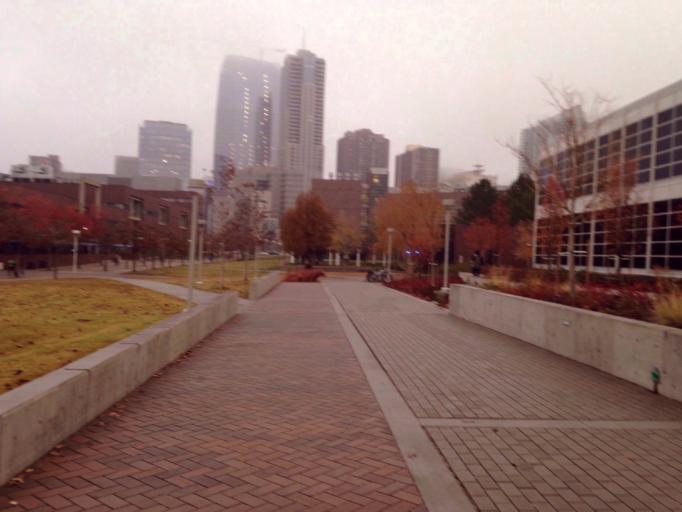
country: US
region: Colorado
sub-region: Denver County
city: Denver
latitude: 39.7439
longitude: -105.0034
